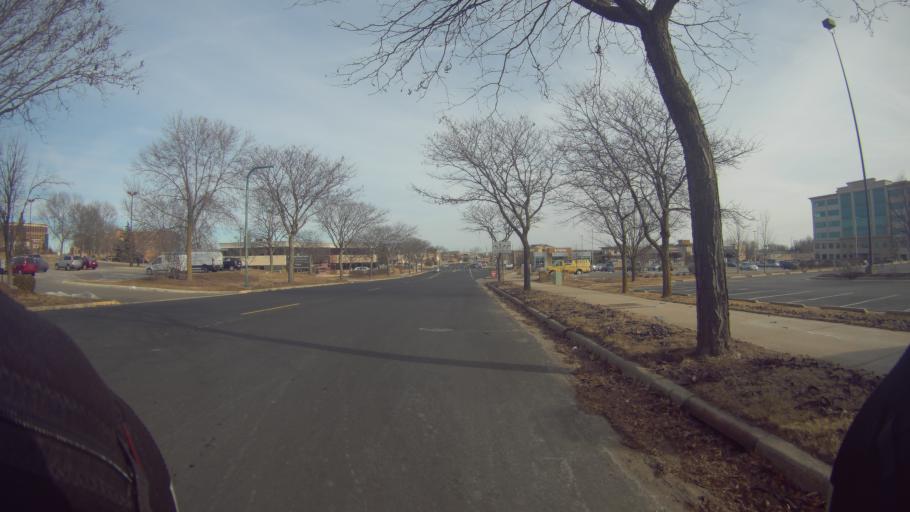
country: US
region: Wisconsin
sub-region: Dane County
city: Middleton
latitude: 43.0885
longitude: -89.5246
